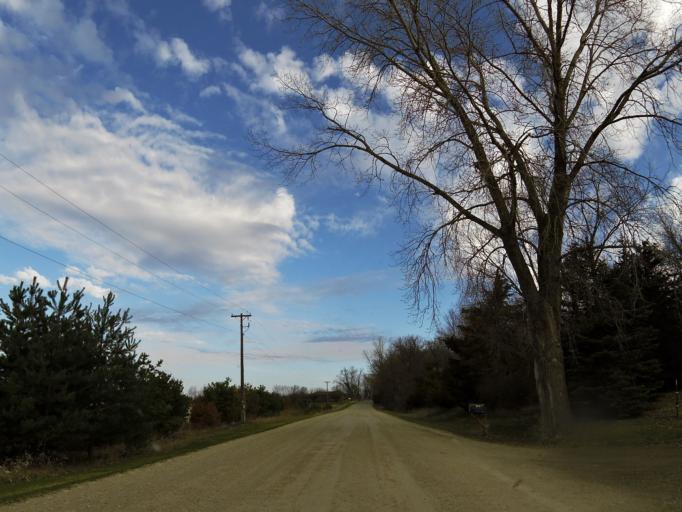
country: US
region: Minnesota
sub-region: Dakota County
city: Hastings
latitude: 44.7698
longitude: -92.8413
